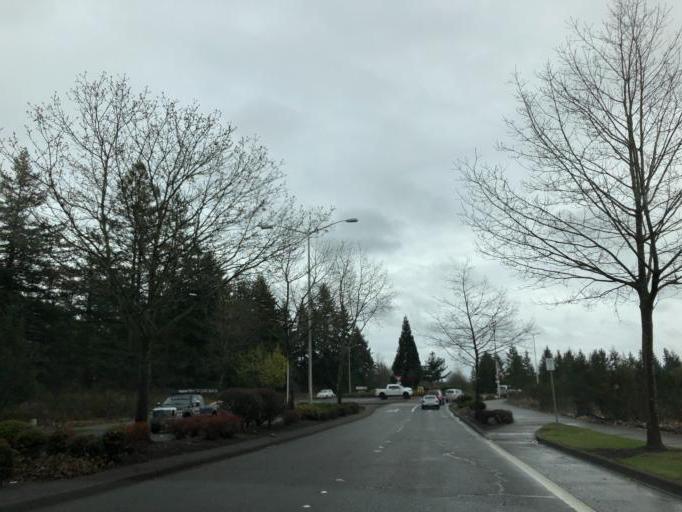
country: US
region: Washington
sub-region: Thurston County
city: Tanglewilde-Thompson Place
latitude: 47.0678
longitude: -122.7695
